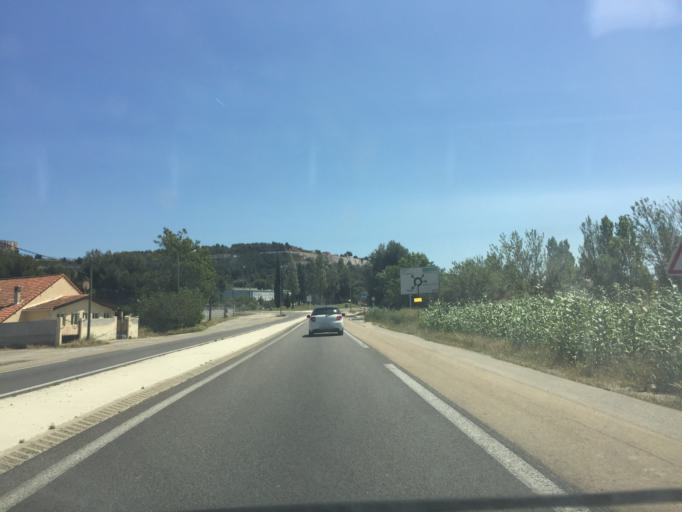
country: FR
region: Provence-Alpes-Cote d'Azur
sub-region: Departement des Bouches-du-Rhone
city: Rognac
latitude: 43.4720
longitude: 5.2301
